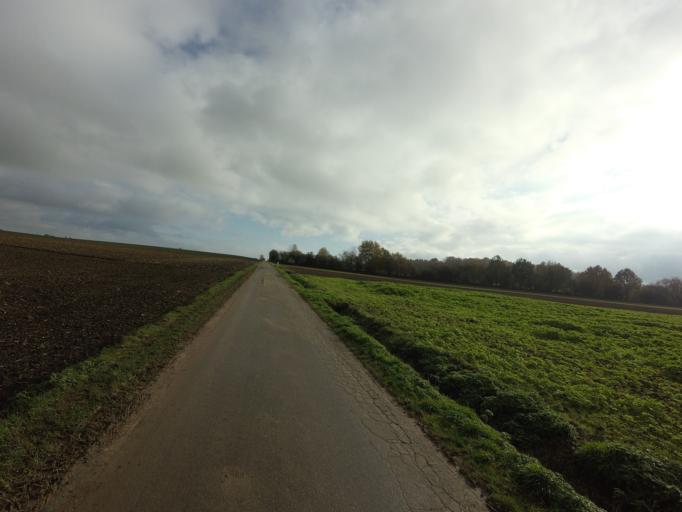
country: NL
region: Limburg
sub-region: Gemeente Vaals
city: Vaals
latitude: 50.7905
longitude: 6.0141
